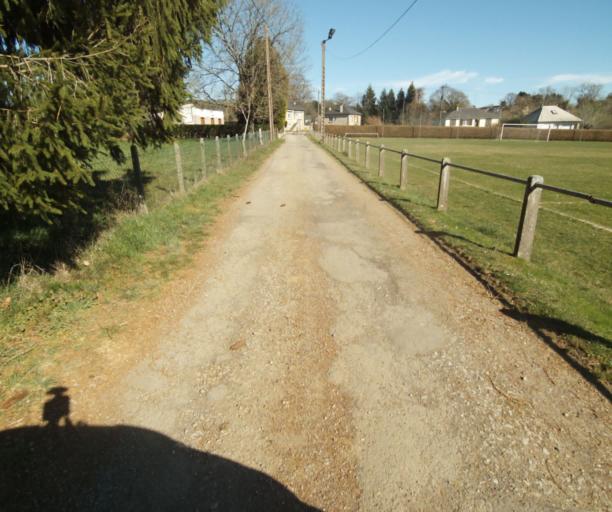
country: FR
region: Limousin
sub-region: Departement de la Correze
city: Chamboulive
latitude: 45.4692
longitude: 1.7332
